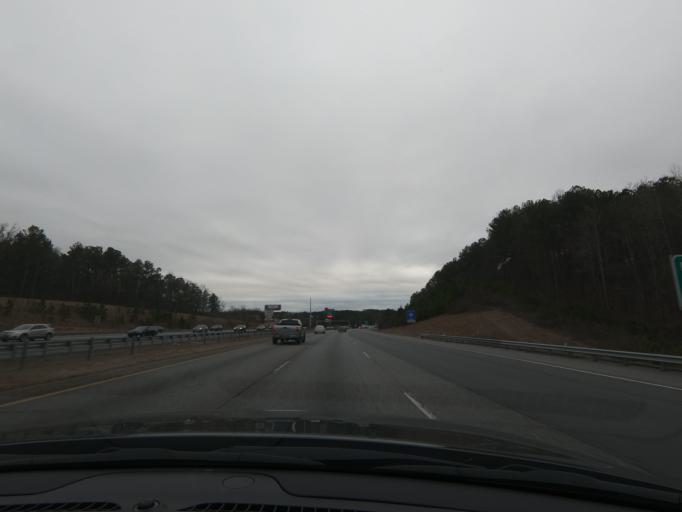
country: US
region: Georgia
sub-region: Cherokee County
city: Holly Springs
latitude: 34.1405
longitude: -84.5202
